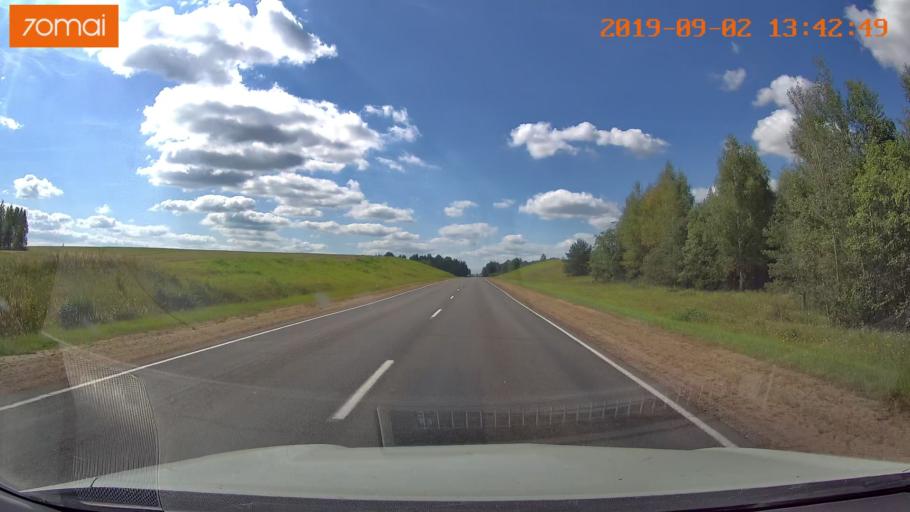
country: BY
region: Mogilev
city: Cherykaw
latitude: 53.5949
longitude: 31.3994
